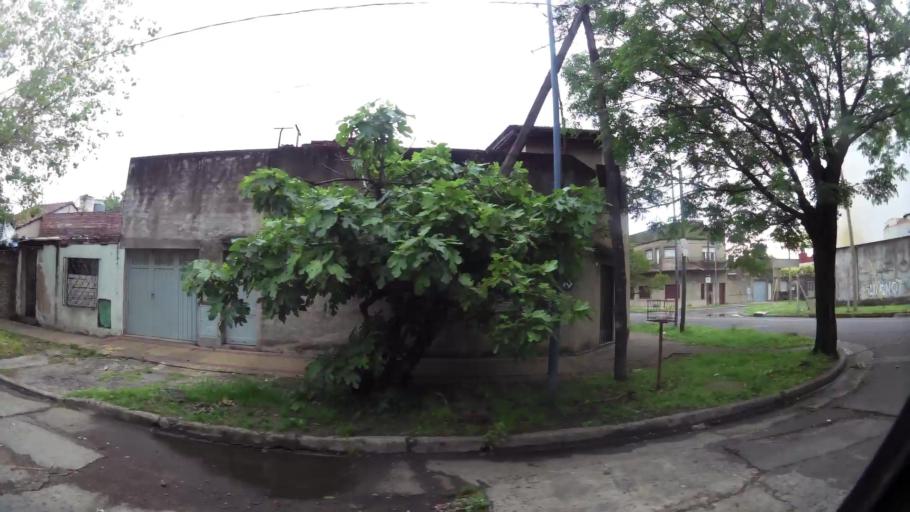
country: AR
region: Buenos Aires
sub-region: Partido de Lanus
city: Lanus
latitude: -34.6998
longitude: -58.3685
